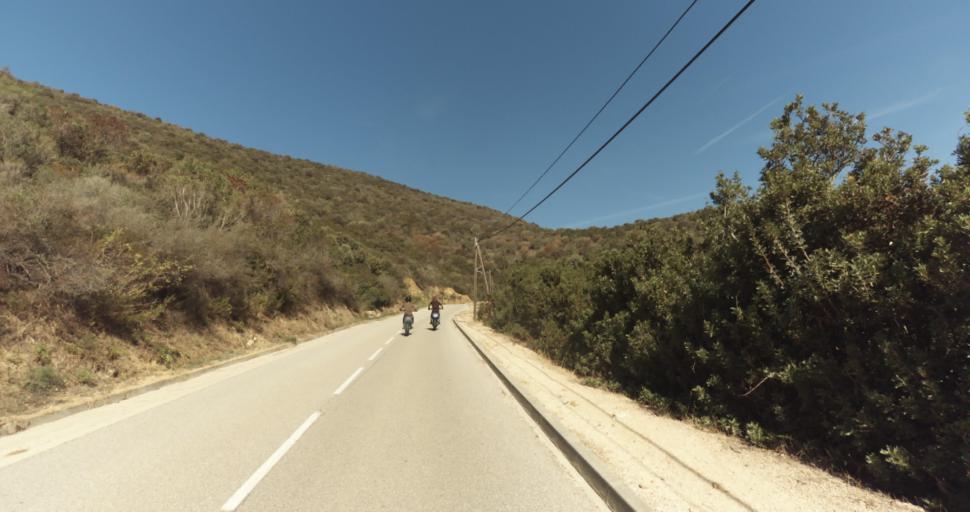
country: FR
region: Corsica
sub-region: Departement de la Corse-du-Sud
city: Ajaccio
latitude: 41.9171
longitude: 8.6419
